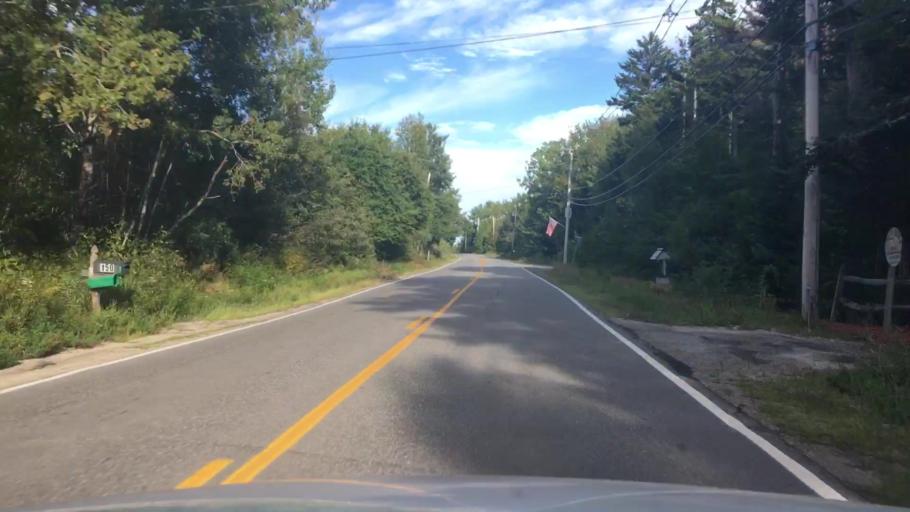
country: US
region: Maine
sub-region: Hancock County
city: Trenton
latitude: 44.4375
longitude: -68.3836
